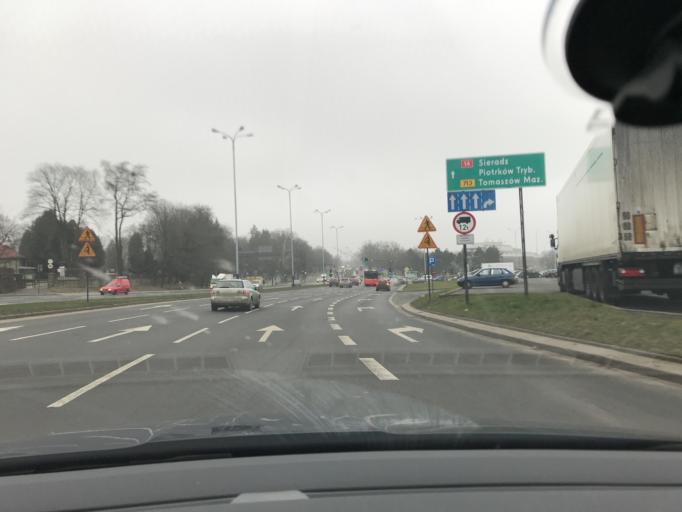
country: PL
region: Lodz Voivodeship
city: Lodz
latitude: 51.7924
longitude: 19.4884
